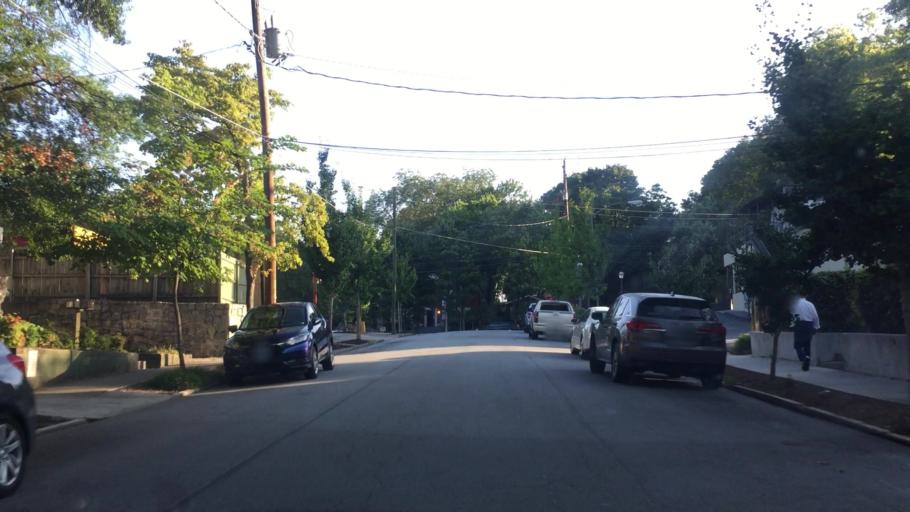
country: US
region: Georgia
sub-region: DeKalb County
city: Druid Hills
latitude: 33.7730
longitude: -84.3573
